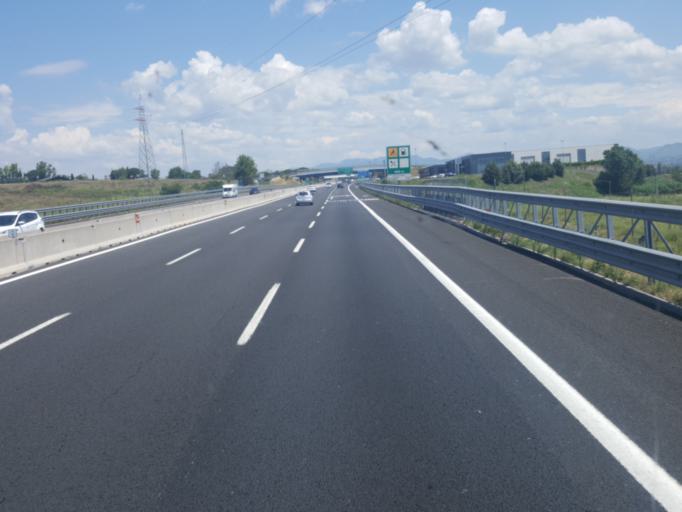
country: IT
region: Latium
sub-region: Citta metropolitana di Roma Capitale
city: Bivio di Capanelle
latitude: 42.1247
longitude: 12.5966
